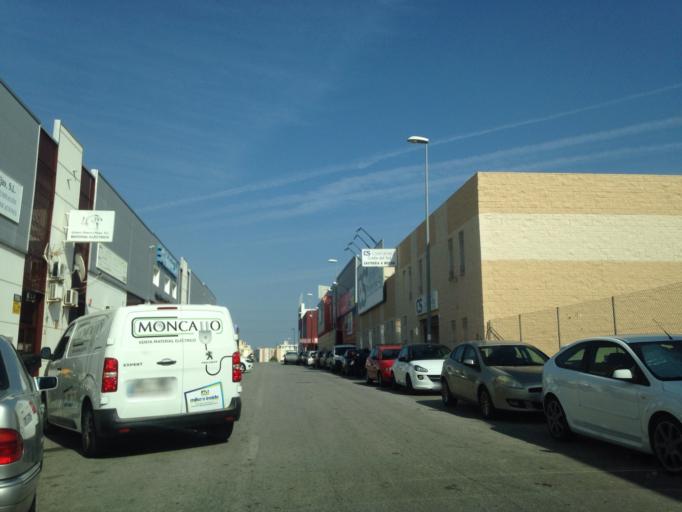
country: ES
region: Andalusia
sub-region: Provincia de Malaga
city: Malaga
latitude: 36.7107
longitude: -4.4702
